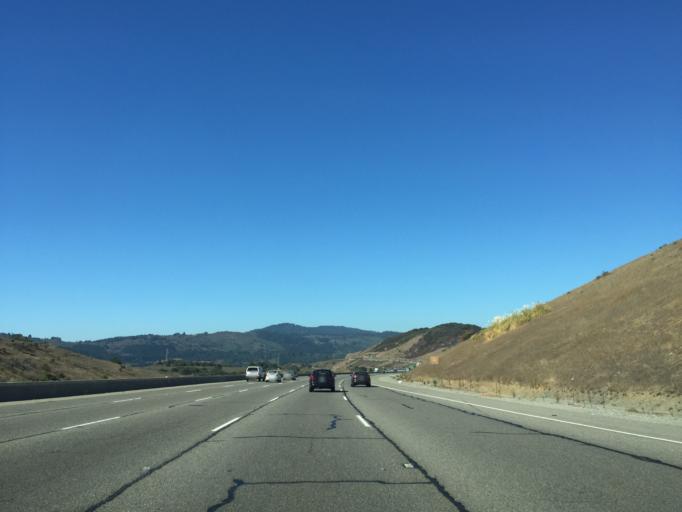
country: US
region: California
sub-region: San Mateo County
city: Belmont
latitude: 37.4959
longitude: -122.3096
